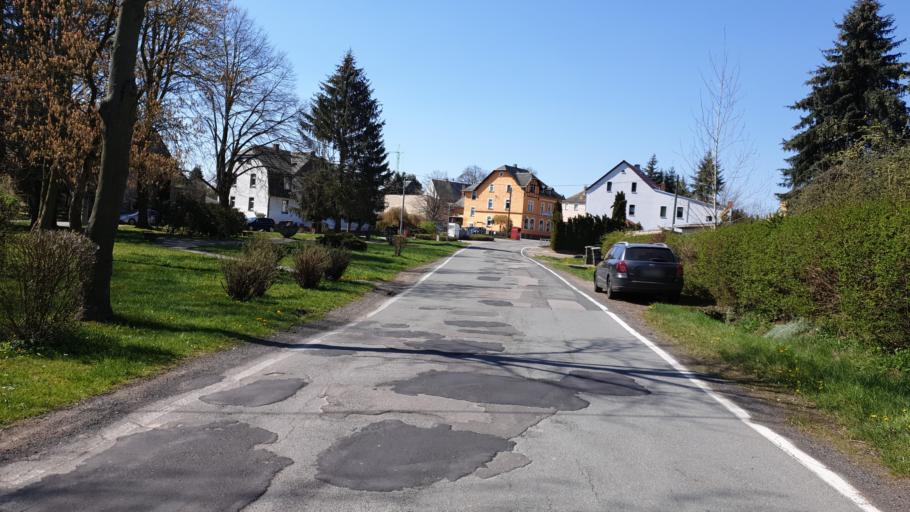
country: DE
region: Saxony
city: Claussnitz
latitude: 50.9094
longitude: 12.8758
